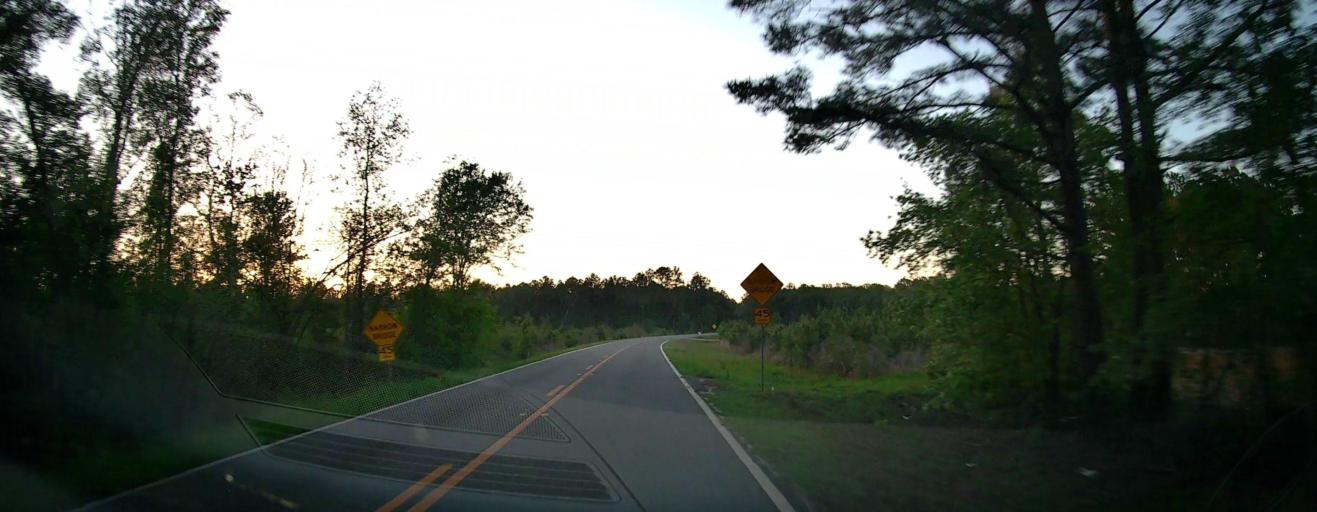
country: US
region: Georgia
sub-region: Wilcox County
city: Rochelle
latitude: 31.7992
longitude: -83.4505
